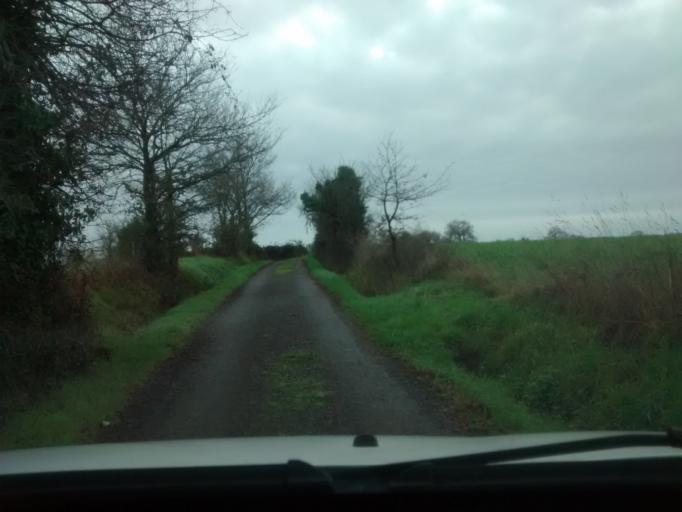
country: FR
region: Brittany
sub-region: Departement d'Ille-et-Vilaine
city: Montgermont
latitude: 48.1349
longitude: -1.7242
